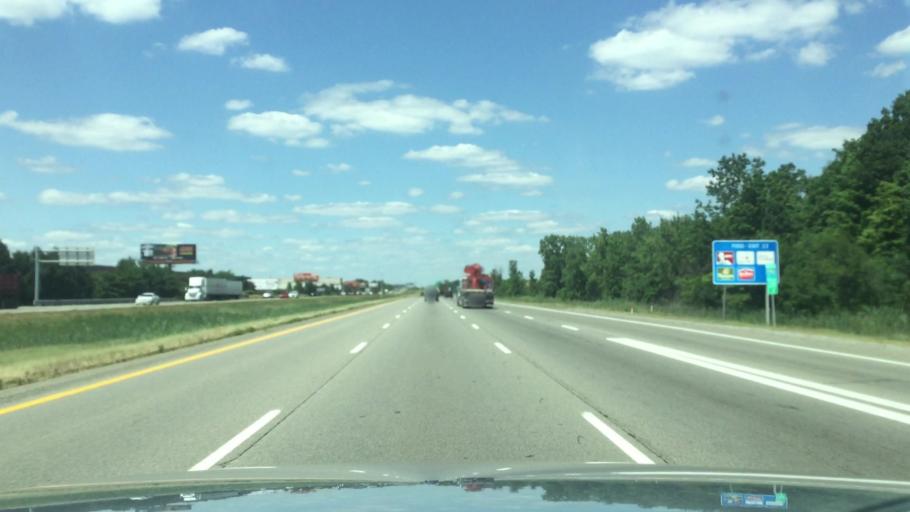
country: US
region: Michigan
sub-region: Wayne County
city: Romulus
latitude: 42.2534
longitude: -83.4398
